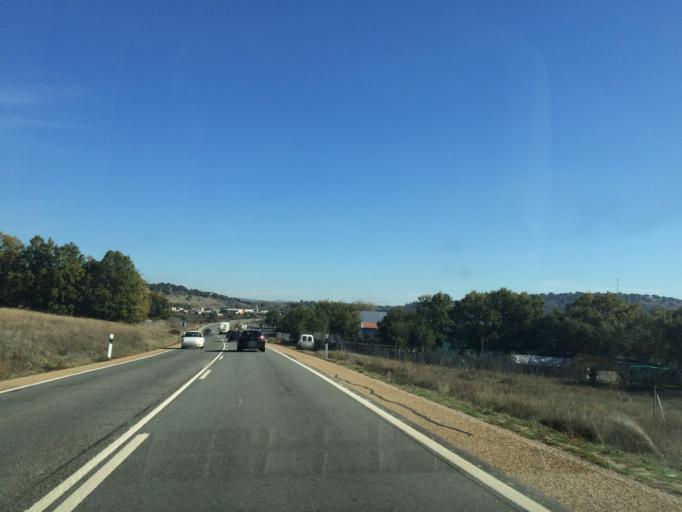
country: ES
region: Madrid
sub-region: Provincia de Madrid
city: Guadalix de la Sierra
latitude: 40.7901
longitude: -3.6994
